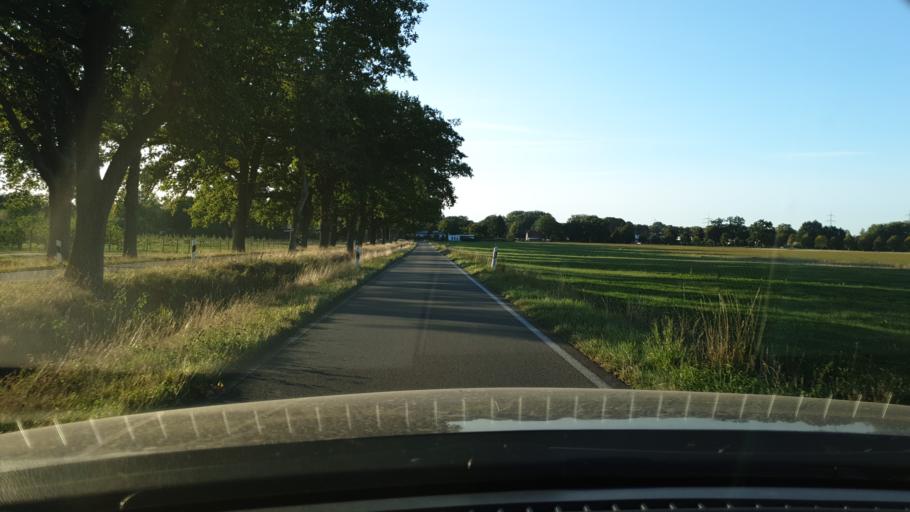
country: DE
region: Mecklenburg-Vorpommern
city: Wittenburg
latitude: 53.4972
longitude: 11.0073
